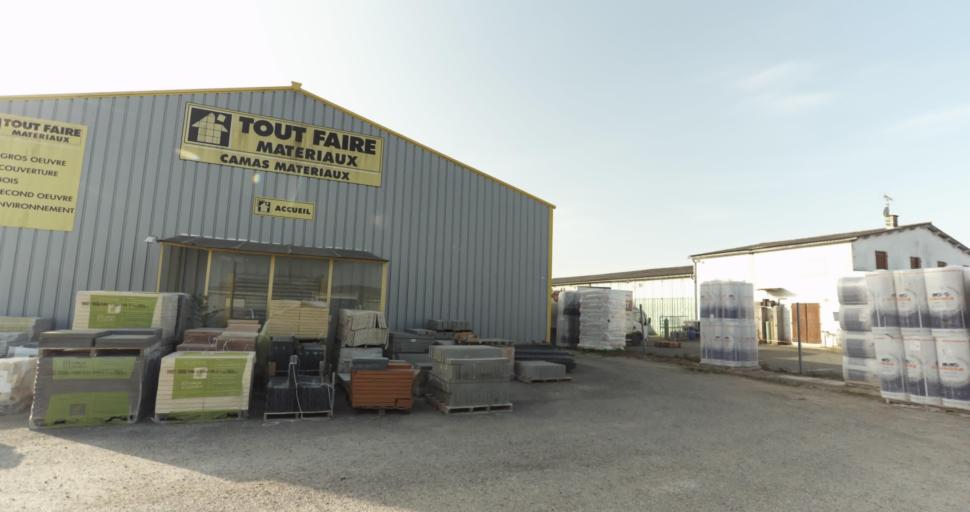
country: FR
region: Midi-Pyrenees
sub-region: Departement du Tarn
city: Saint-Sulpice-la-Pointe
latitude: 43.7706
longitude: 1.6747
